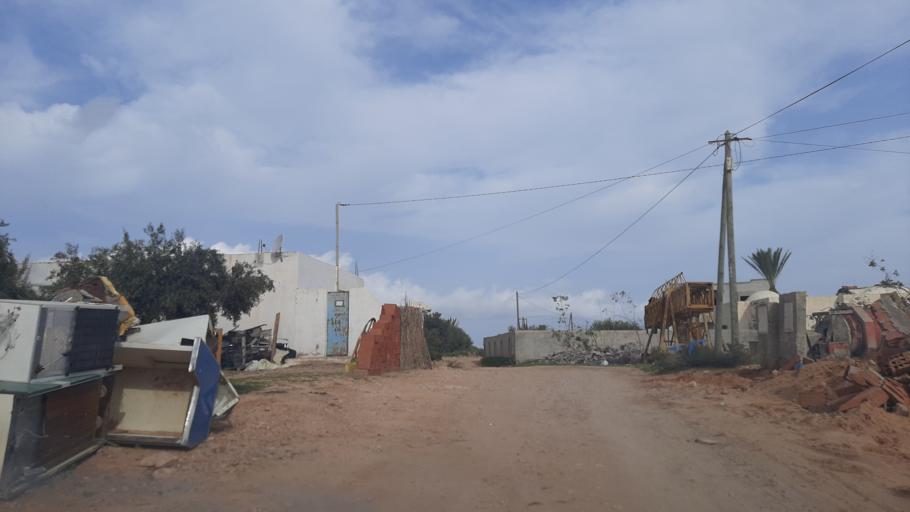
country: TN
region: Madanin
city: Midoun
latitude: 33.8065
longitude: 11.0239
